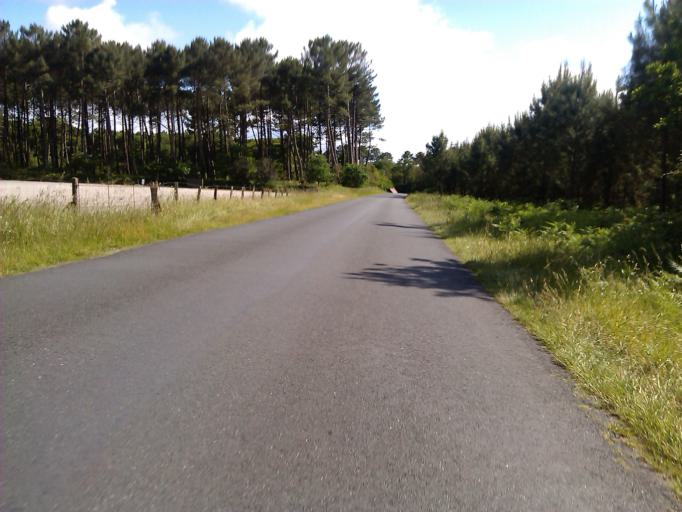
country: FR
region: Aquitaine
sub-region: Departement des Landes
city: Leon
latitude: 43.8599
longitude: -1.3576
